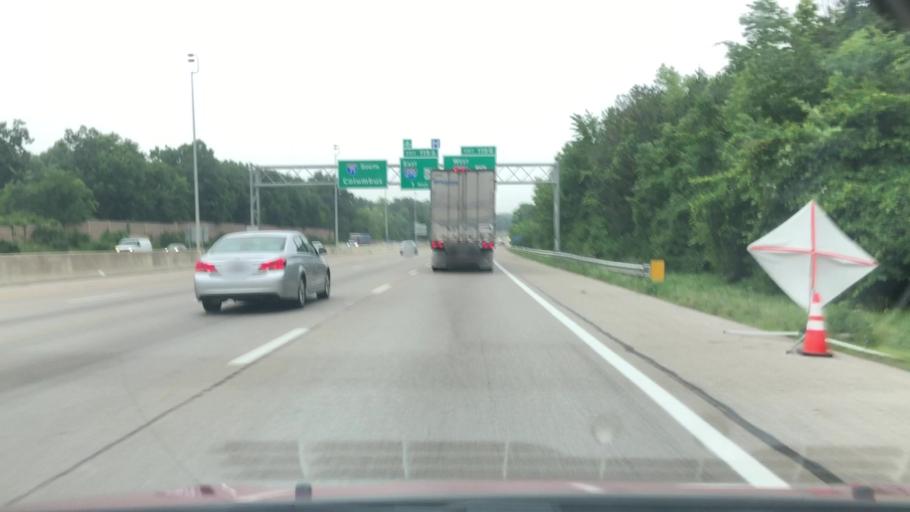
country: US
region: Ohio
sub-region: Franklin County
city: Westerville
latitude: 40.1247
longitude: -82.9725
